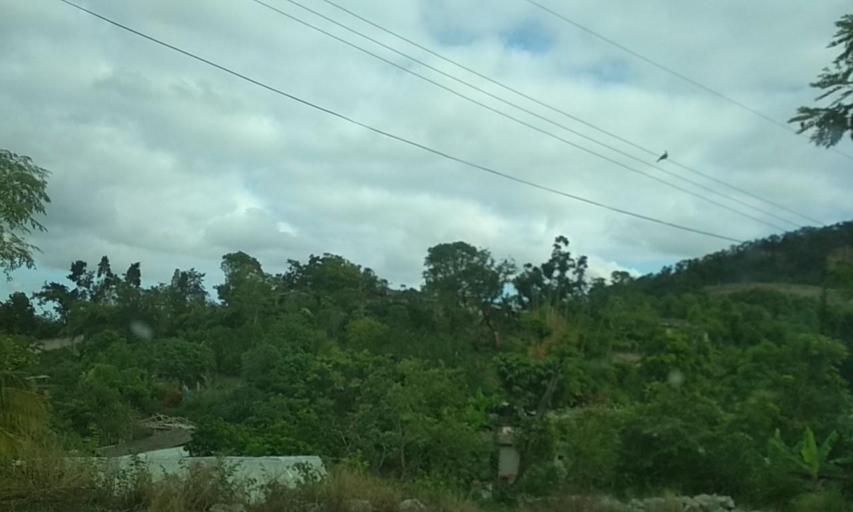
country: MX
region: Veracruz
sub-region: Papantla
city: Polutla
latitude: 20.5743
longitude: -97.2530
